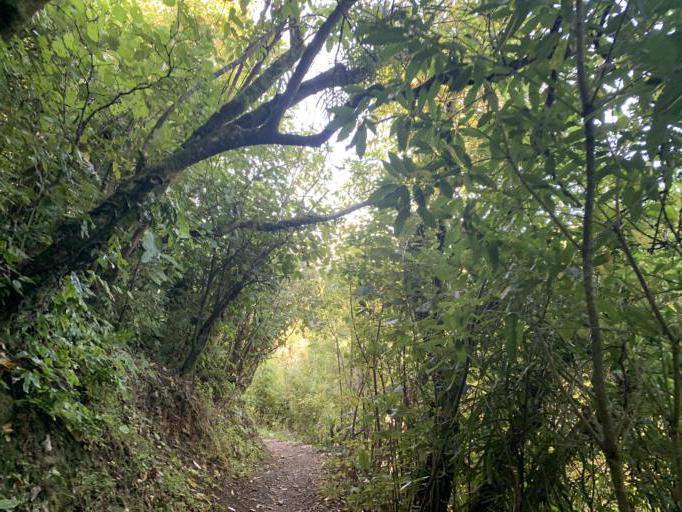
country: NZ
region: Wellington
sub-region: Wellington City
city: Kelburn
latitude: -41.2974
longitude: 174.7554
